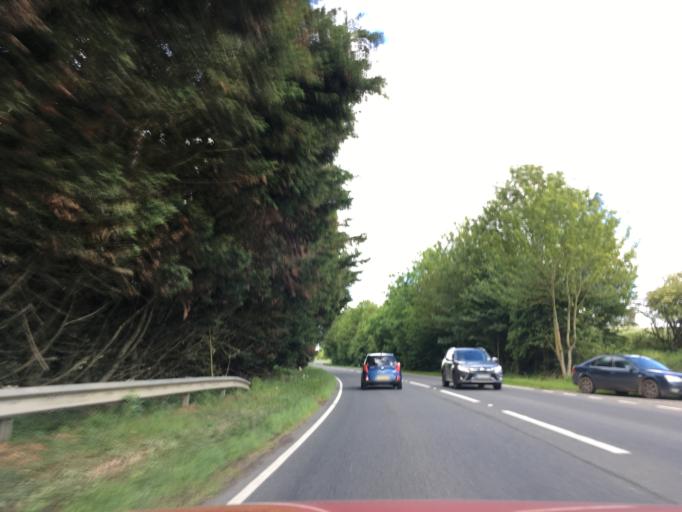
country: GB
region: England
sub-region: Oxfordshire
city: Burford
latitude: 51.7892
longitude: -1.6423
